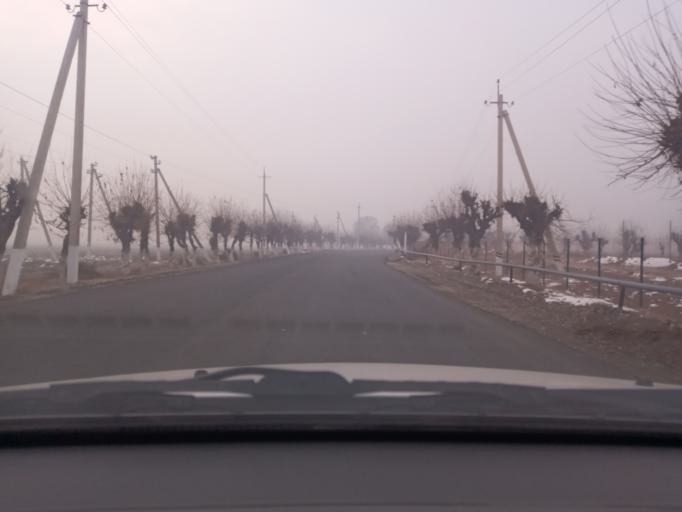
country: UZ
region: Namangan
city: Pop
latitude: 40.8708
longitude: 71.1468
